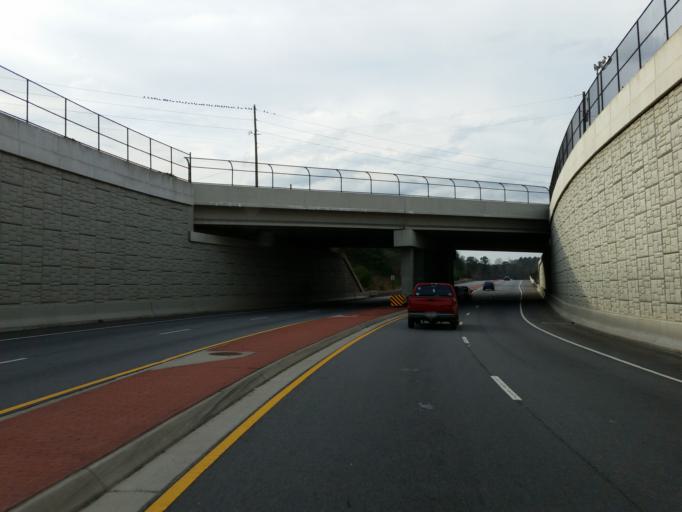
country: US
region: Georgia
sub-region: Cobb County
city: Fair Oaks
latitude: 33.8963
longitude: -84.5904
